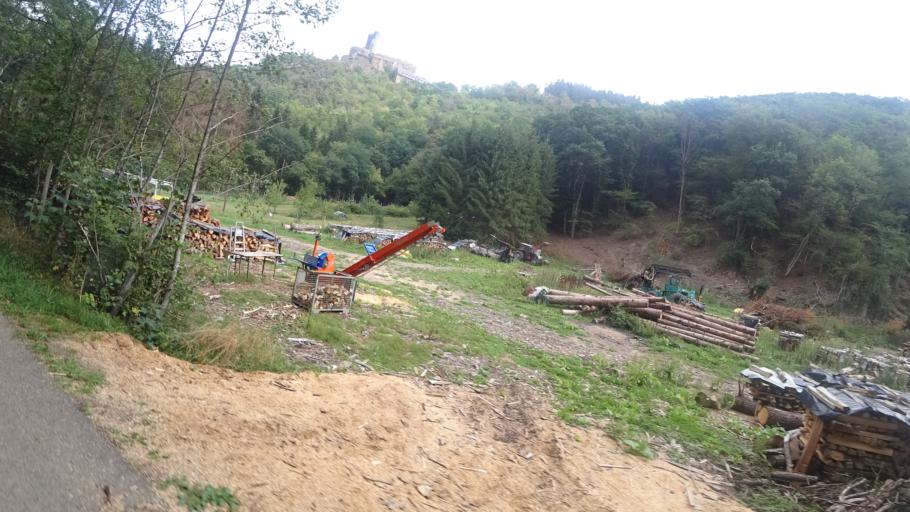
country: DE
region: Rheinland-Pfalz
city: Morshausen
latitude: 50.2081
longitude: 7.4536
